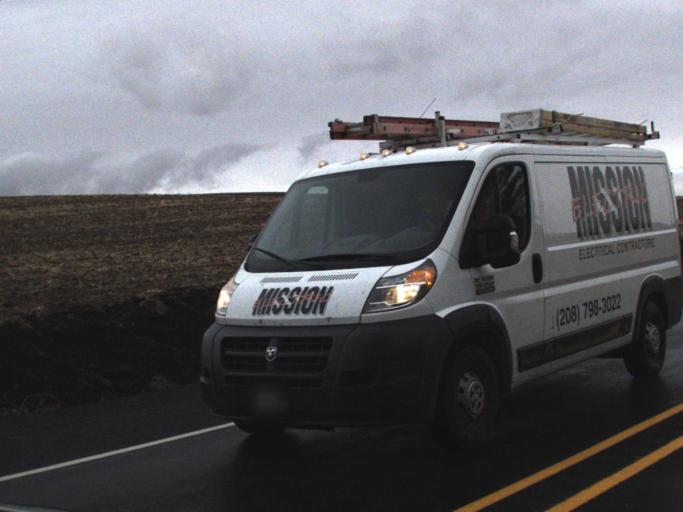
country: US
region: Washington
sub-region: Whitman County
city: Colfax
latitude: 46.8470
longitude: -117.4836
